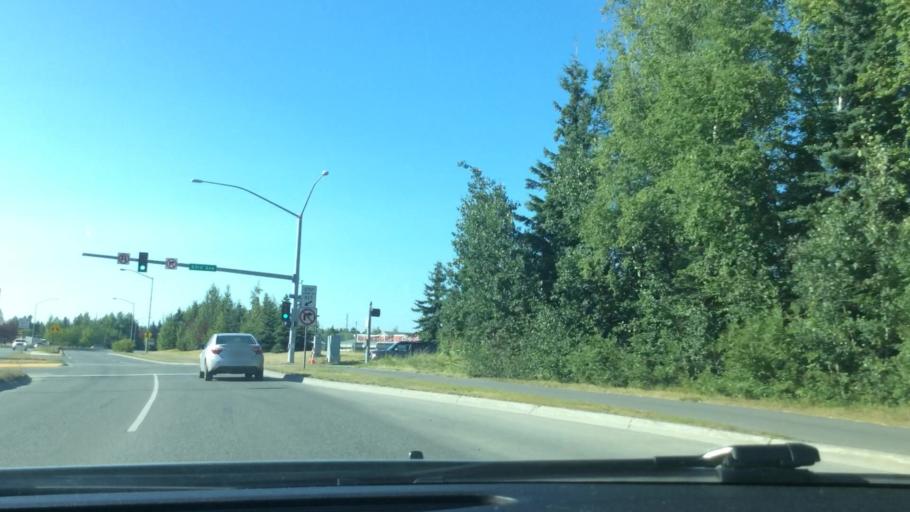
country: US
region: Alaska
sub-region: Anchorage Municipality
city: Anchorage
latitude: 61.1630
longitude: -149.8348
